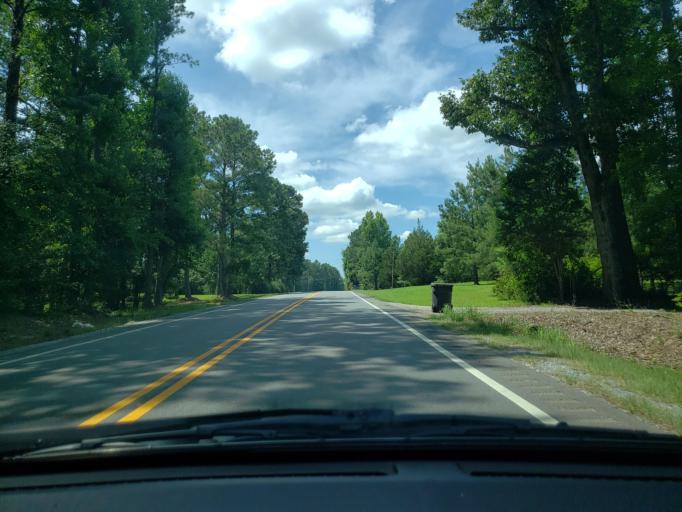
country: US
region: Alabama
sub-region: Elmore County
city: Eclectic
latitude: 32.6303
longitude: -85.9522
